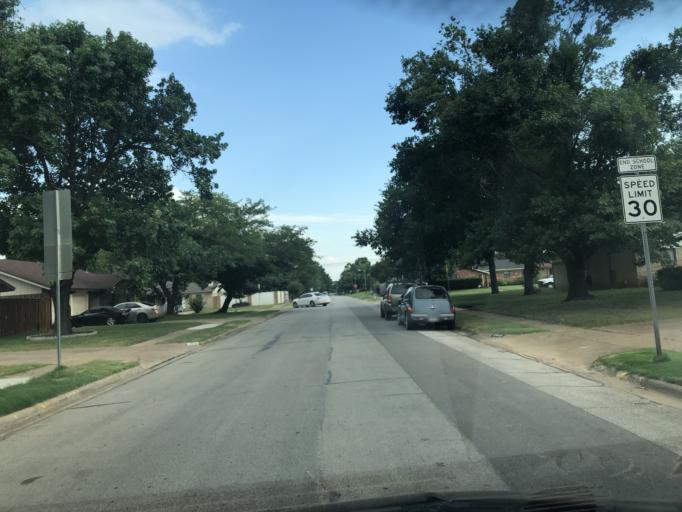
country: US
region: Texas
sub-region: Dallas County
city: Irving
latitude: 32.7905
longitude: -96.9737
